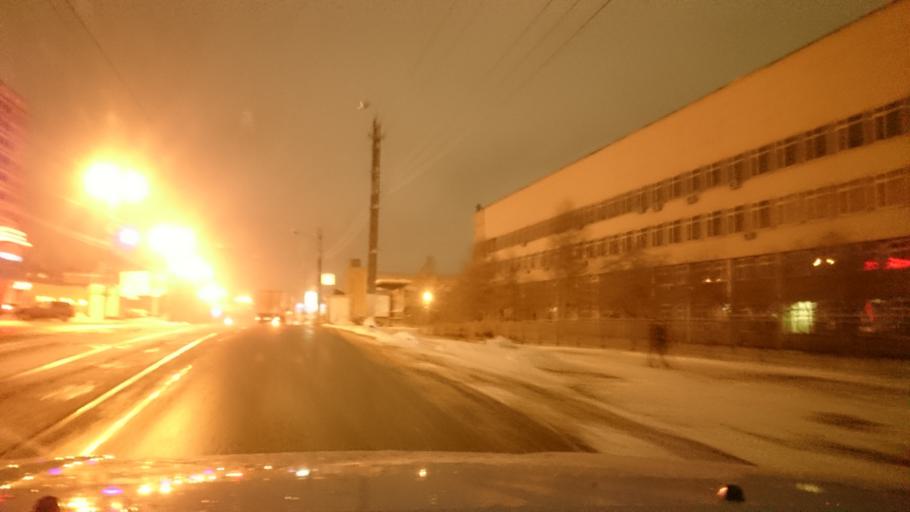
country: RU
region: Tula
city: Tula
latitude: 54.2140
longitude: 37.6166
